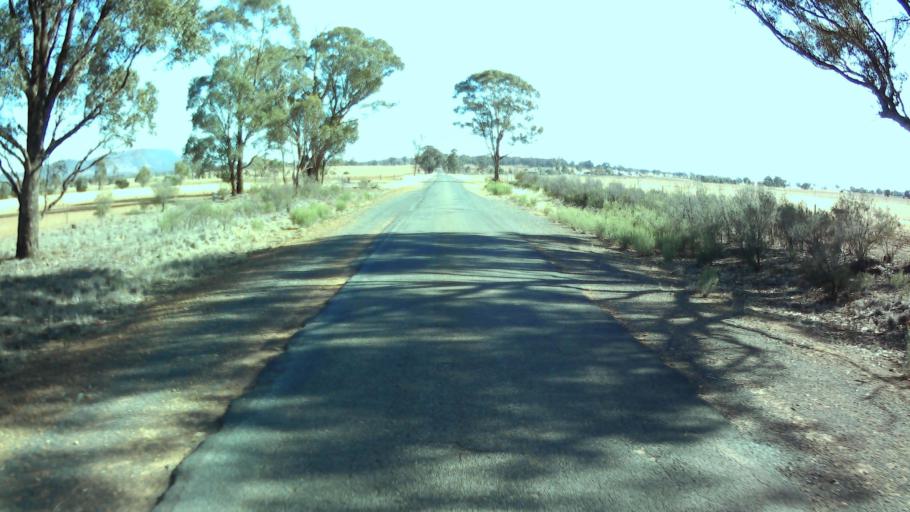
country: AU
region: New South Wales
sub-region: Weddin
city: Grenfell
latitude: -33.8003
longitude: 147.9559
